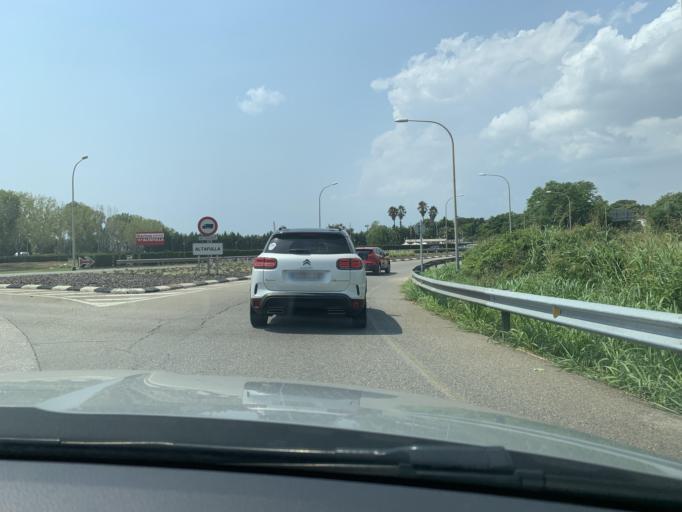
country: ES
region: Catalonia
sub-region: Provincia de Tarragona
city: Altafulla
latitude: 41.1413
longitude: 1.3857
